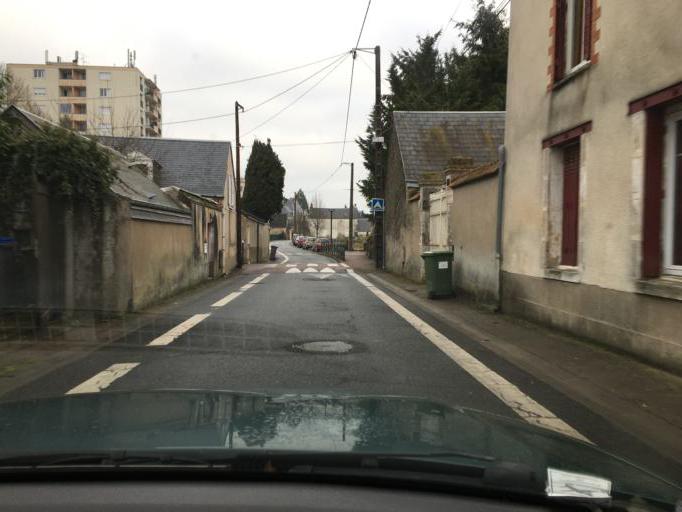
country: FR
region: Centre
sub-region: Departement du Loiret
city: Olivet
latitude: 47.8719
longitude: 1.9055
